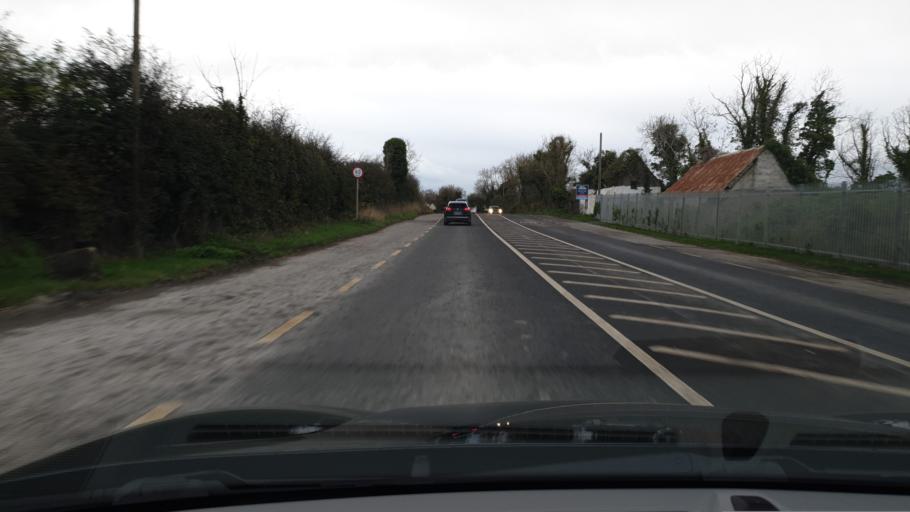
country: IE
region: Leinster
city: Lusk
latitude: 53.5141
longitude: -6.1918
